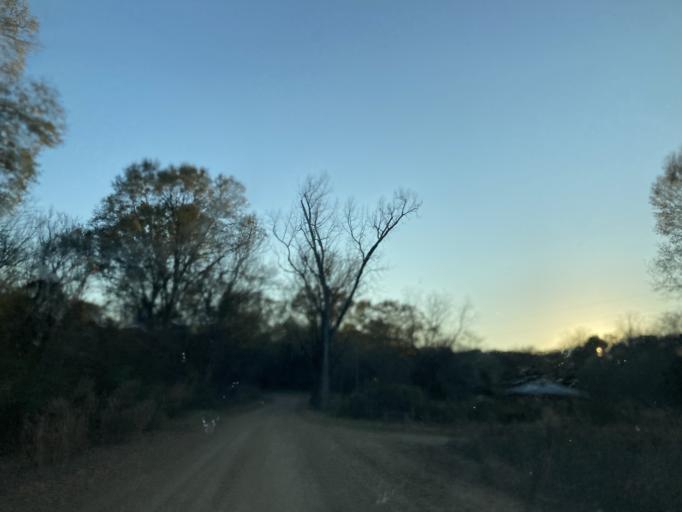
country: US
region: Mississippi
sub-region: Yazoo County
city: Yazoo City
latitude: 32.9702
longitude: -90.2677
